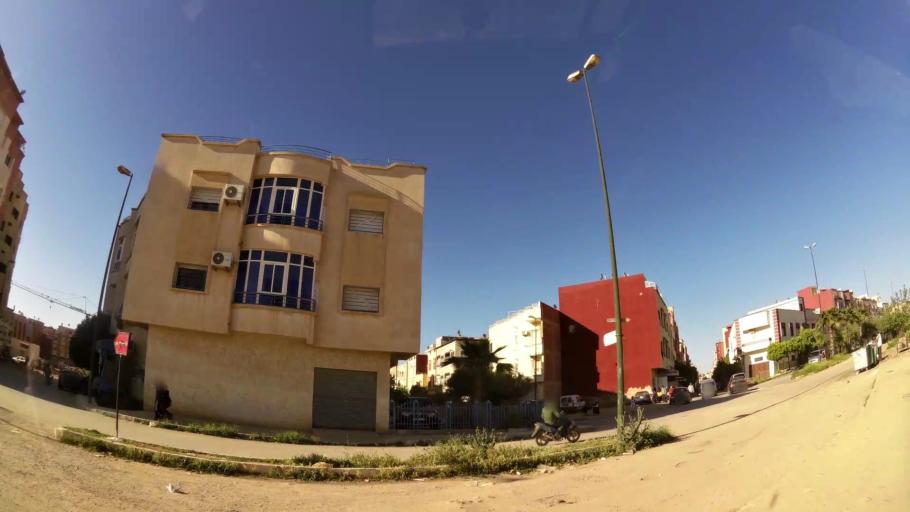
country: MA
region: Meknes-Tafilalet
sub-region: Meknes
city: Meknes
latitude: 33.8885
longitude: -5.5094
